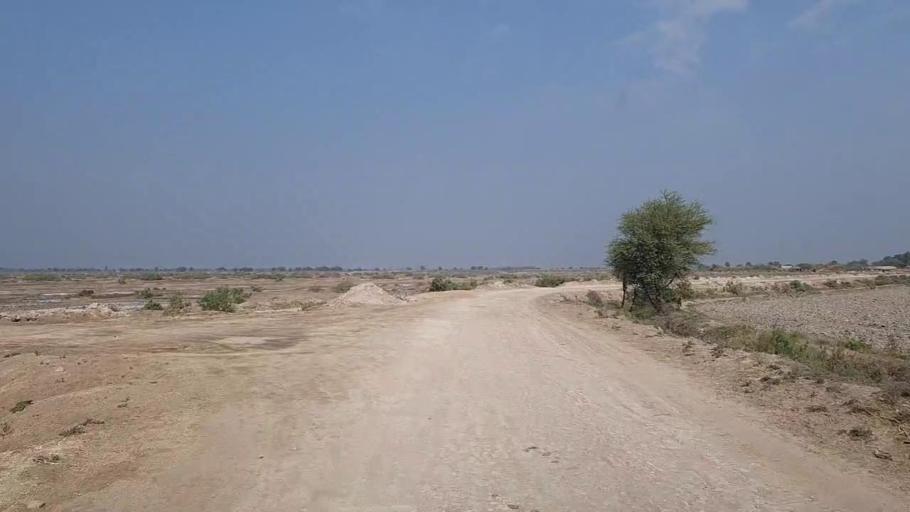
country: PK
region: Sindh
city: Mirwah Gorchani
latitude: 25.3785
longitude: 69.0461
